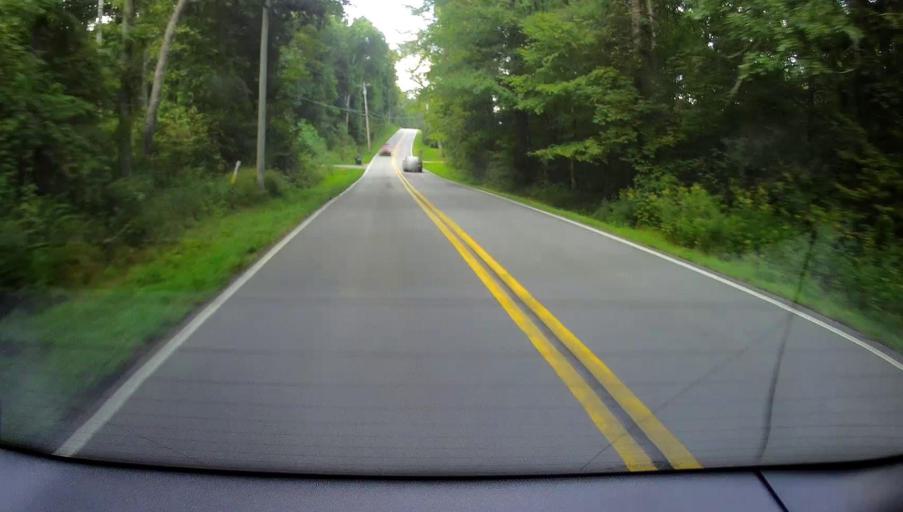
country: US
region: Georgia
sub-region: Catoosa County
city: Ringgold
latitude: 34.9173
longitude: -85.0863
